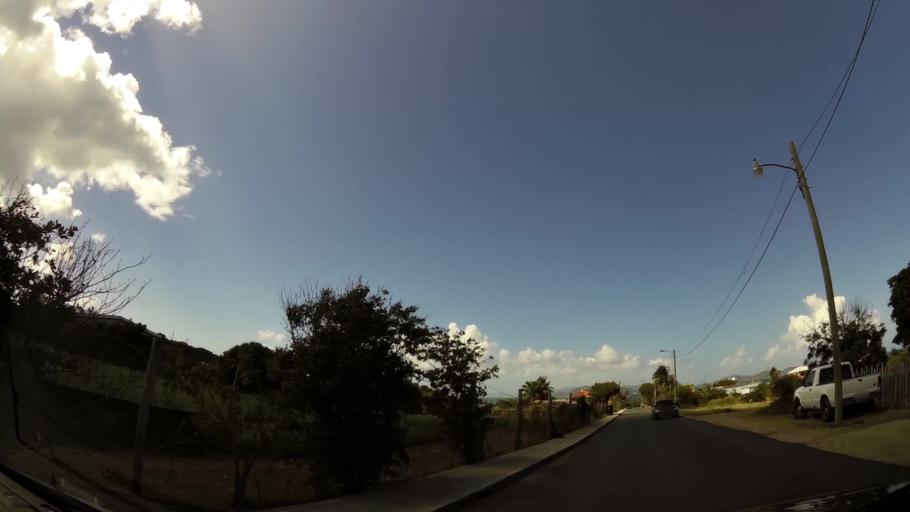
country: VG
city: Tortola
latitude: 18.4494
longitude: -64.4311
